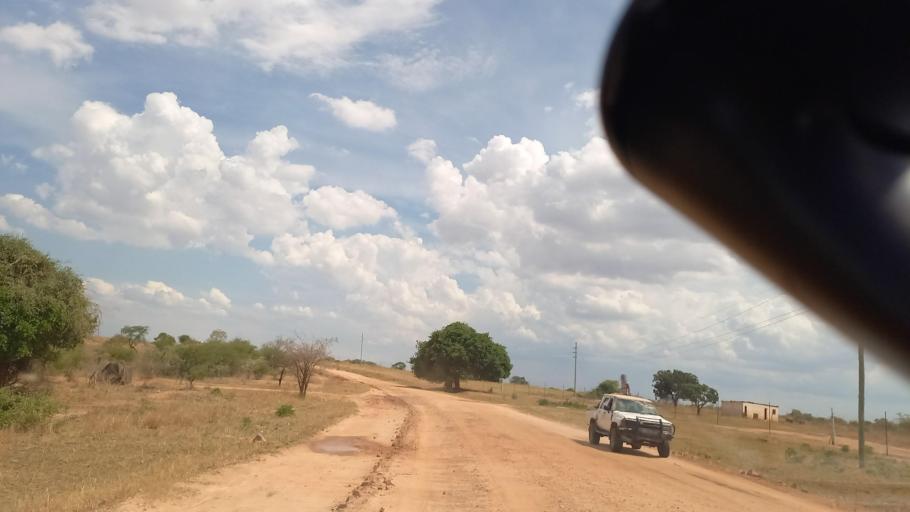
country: ZM
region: Southern
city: Nakambala
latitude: -16.1046
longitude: 28.0214
